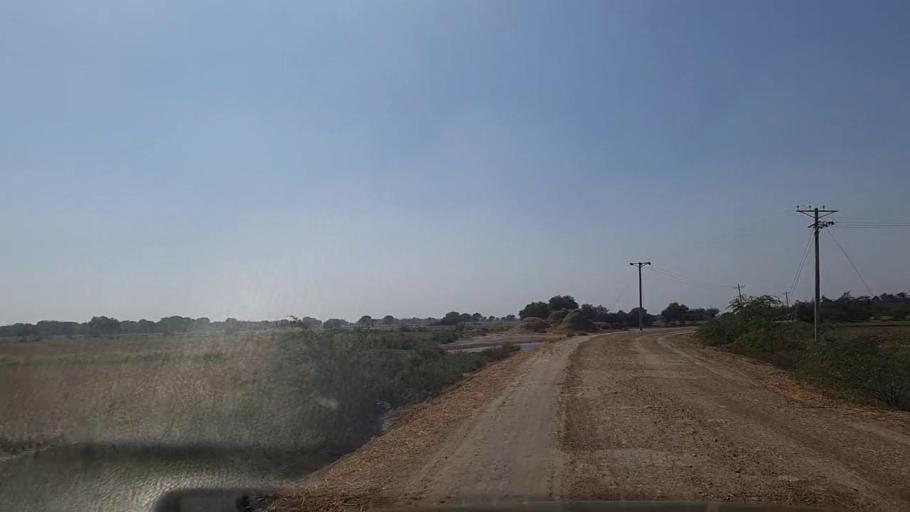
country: PK
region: Sindh
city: Daro Mehar
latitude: 24.8337
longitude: 68.1791
